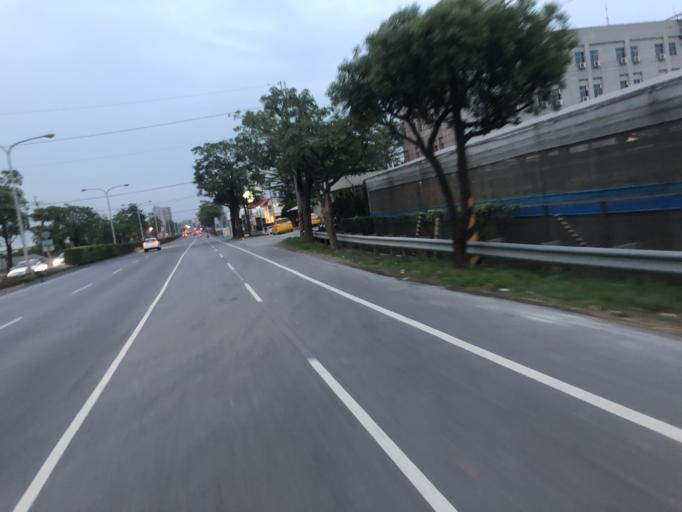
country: TW
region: Taiwan
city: Yujing
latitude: 23.1152
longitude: 120.3185
